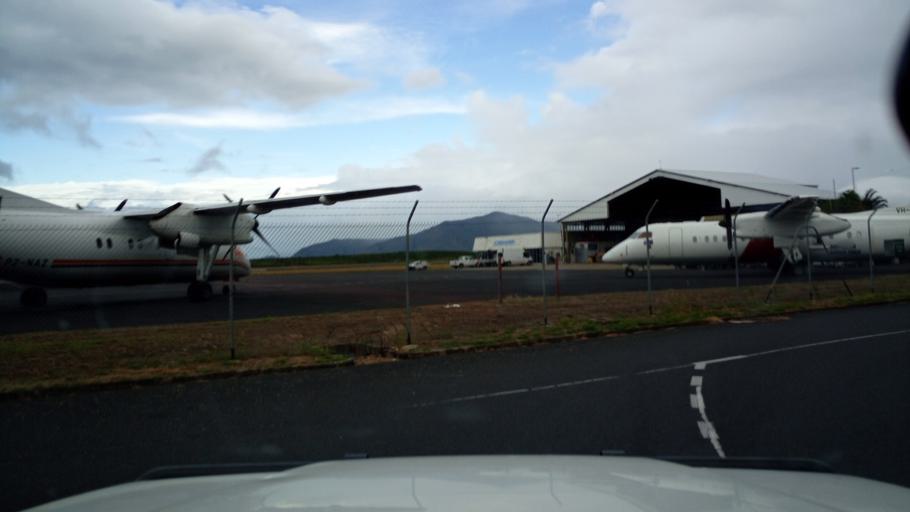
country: AU
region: Queensland
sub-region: Cairns
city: Cairns
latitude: -16.8848
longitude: 145.7492
